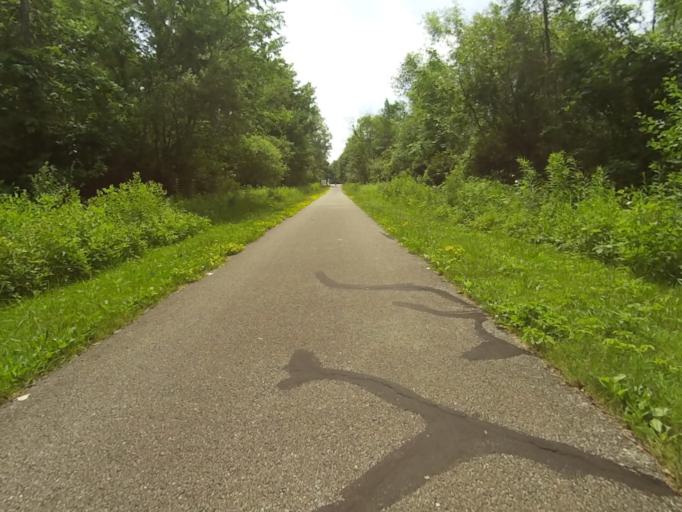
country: US
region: Ohio
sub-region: Summit County
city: Hudson
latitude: 41.2071
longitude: -81.4531
